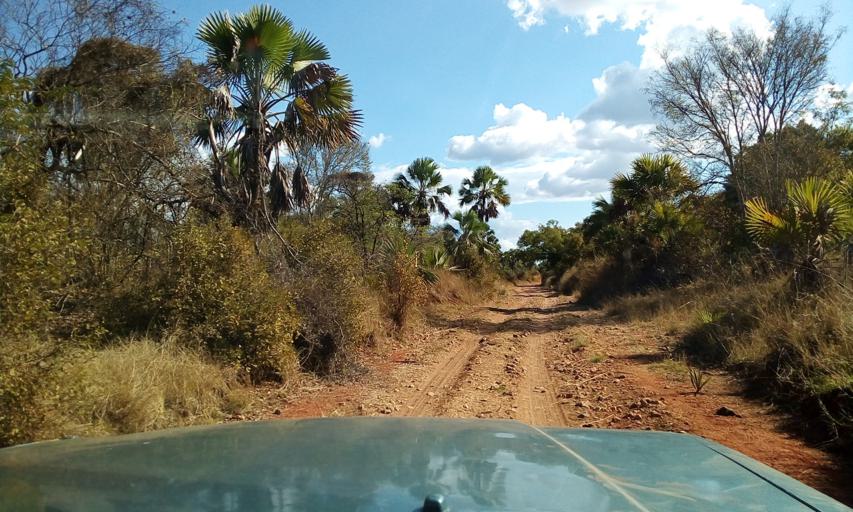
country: MG
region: Boeny
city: Mahajanga
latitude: -16.0597
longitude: 45.7985
